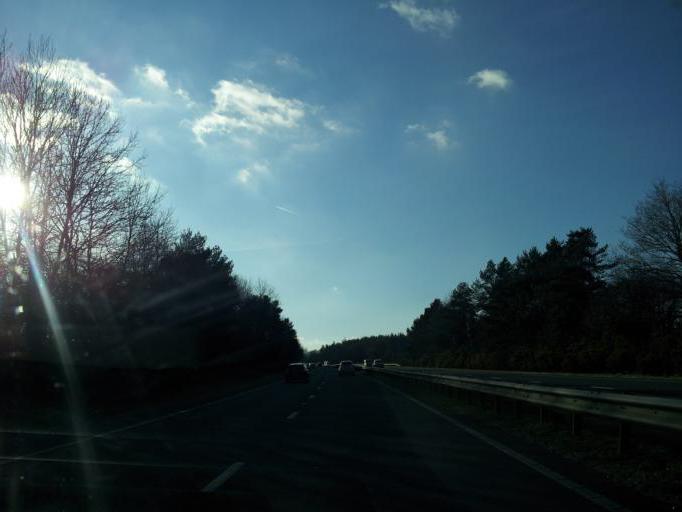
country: GB
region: England
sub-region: Devon
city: Crediton
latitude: 50.7312
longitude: -3.7417
